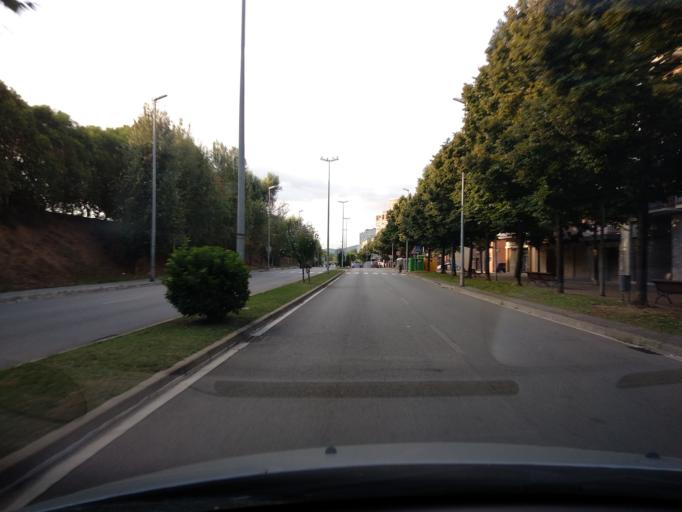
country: ES
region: Catalonia
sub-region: Provincia de Barcelona
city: Granollers
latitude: 41.5988
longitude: 2.2902
